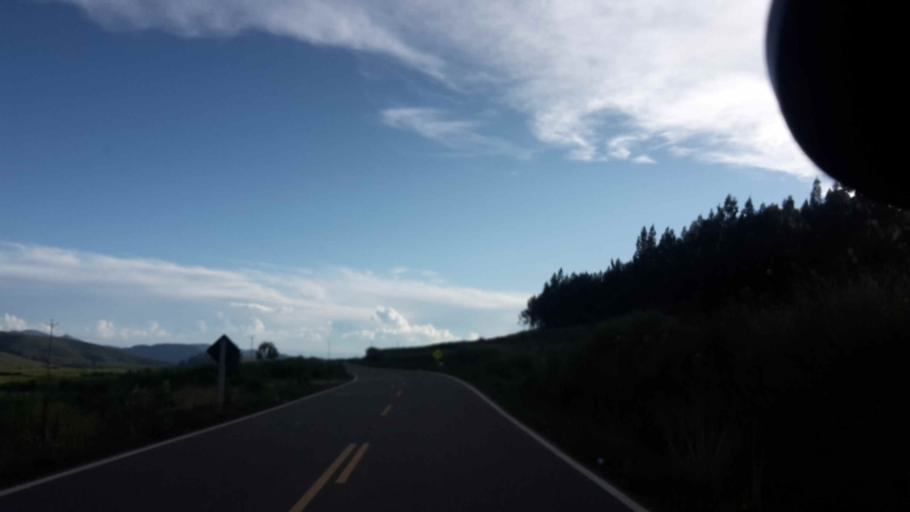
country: BO
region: Cochabamba
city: Arani
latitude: -17.5548
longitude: -65.6961
